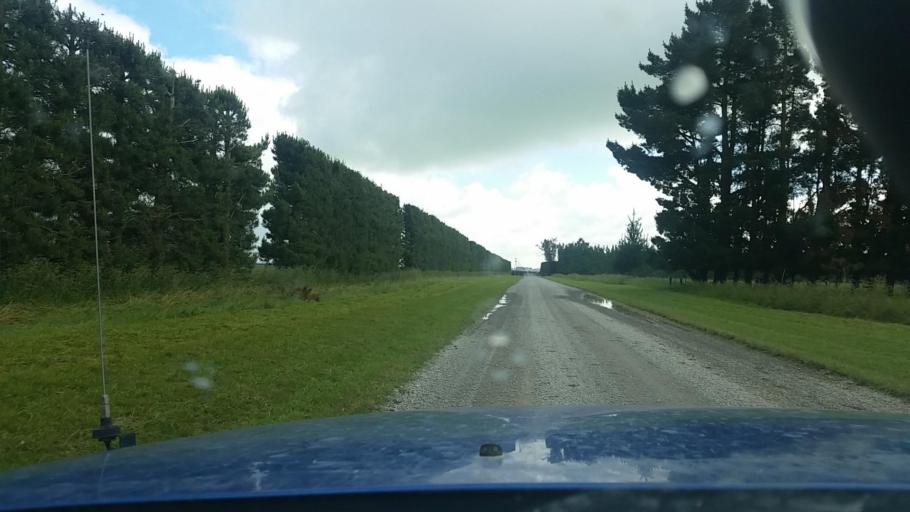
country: NZ
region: Canterbury
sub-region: Ashburton District
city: Tinwald
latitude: -43.9928
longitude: 171.3960
